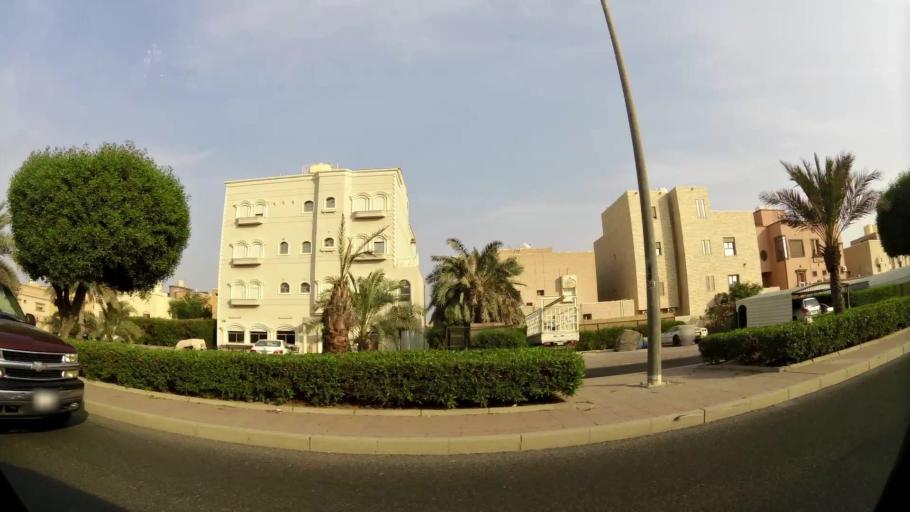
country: KW
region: Mubarak al Kabir
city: Sabah as Salim
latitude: 29.2284
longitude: 48.0605
